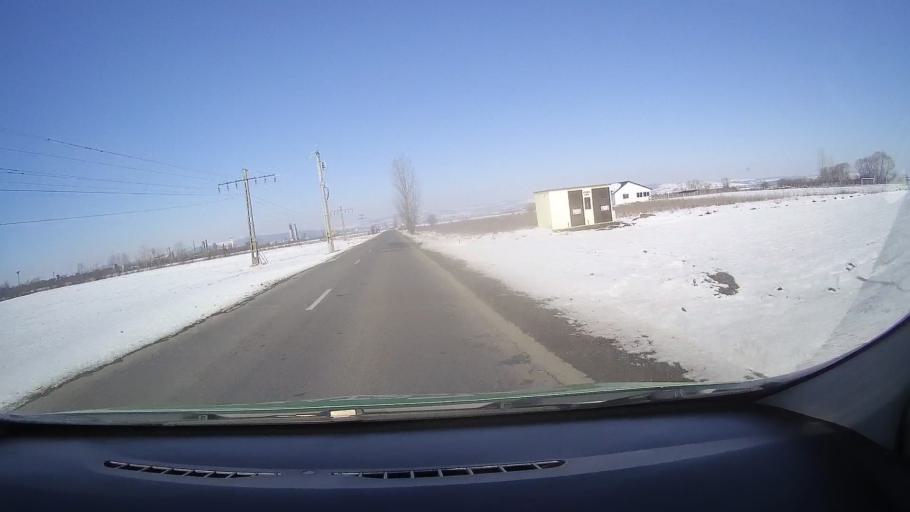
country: RO
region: Brasov
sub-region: Comuna Harseni
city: Harseni
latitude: 45.7958
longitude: 24.9946
